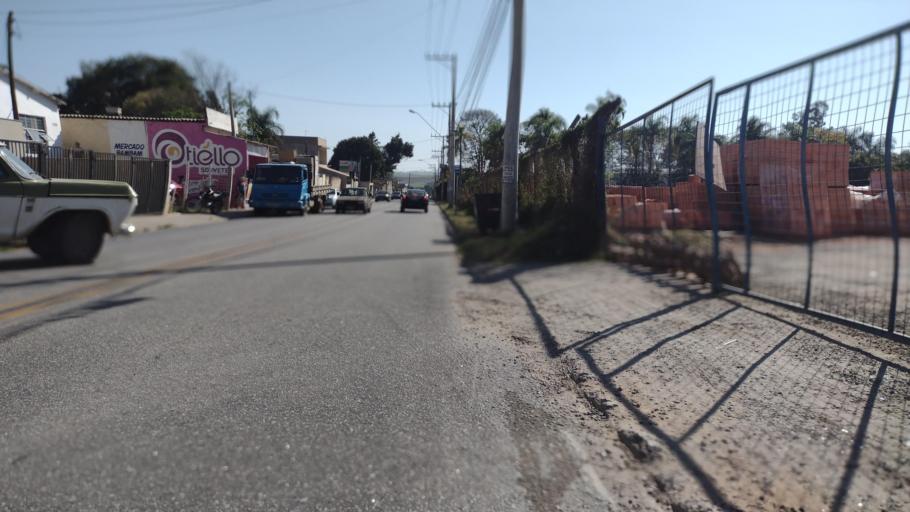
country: BR
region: Sao Paulo
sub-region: Sorocaba
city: Sorocaba
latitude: -23.4186
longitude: -47.4805
